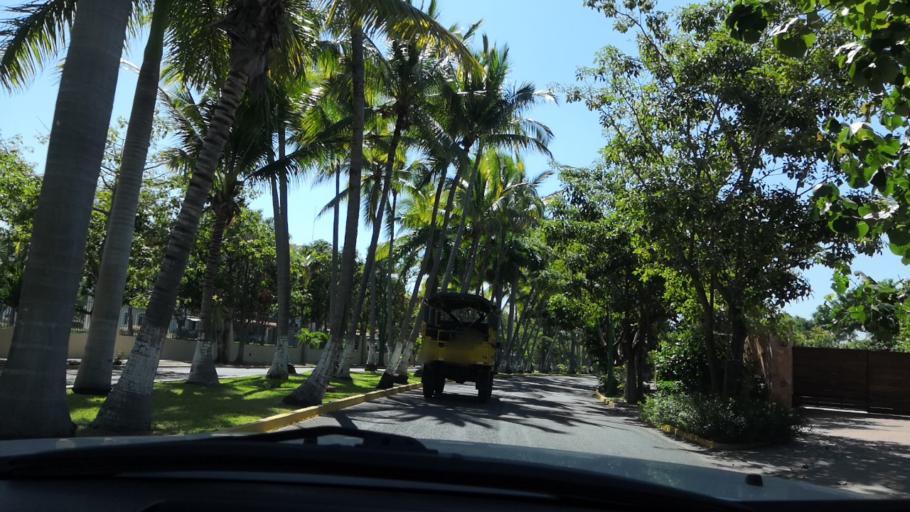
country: MX
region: Nayarit
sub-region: Bahia de Banderas
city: Las Jarretaderas
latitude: 20.6980
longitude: -105.2903
